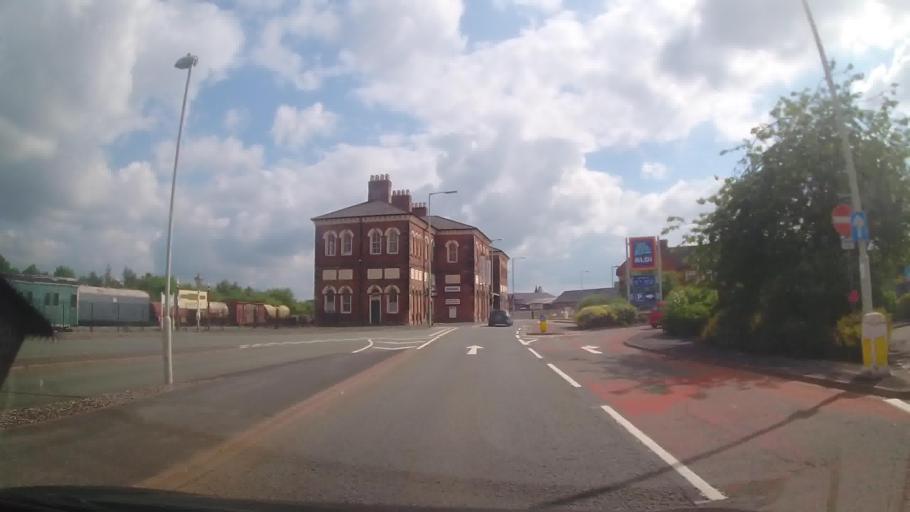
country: GB
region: England
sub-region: Shropshire
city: Oswestry
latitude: 52.8620
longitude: -3.0500
